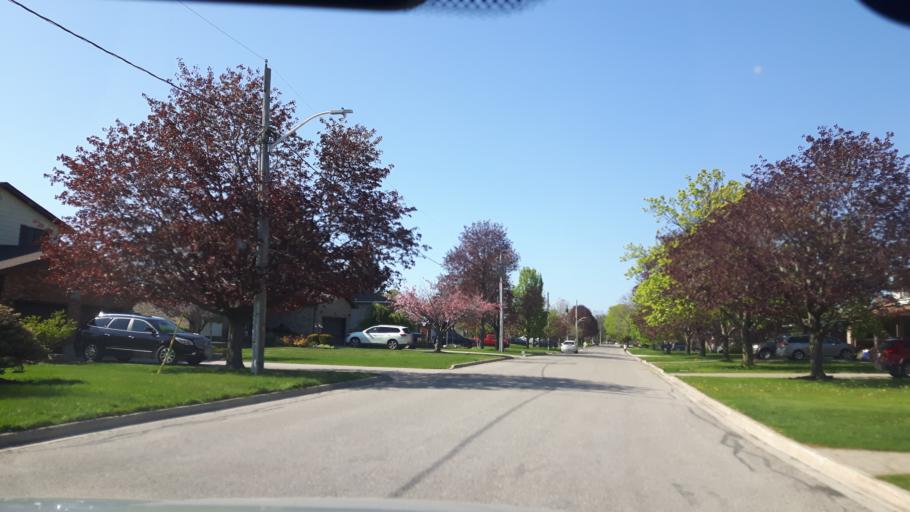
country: CA
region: Ontario
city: Goderich
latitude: 43.7317
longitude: -81.7214
